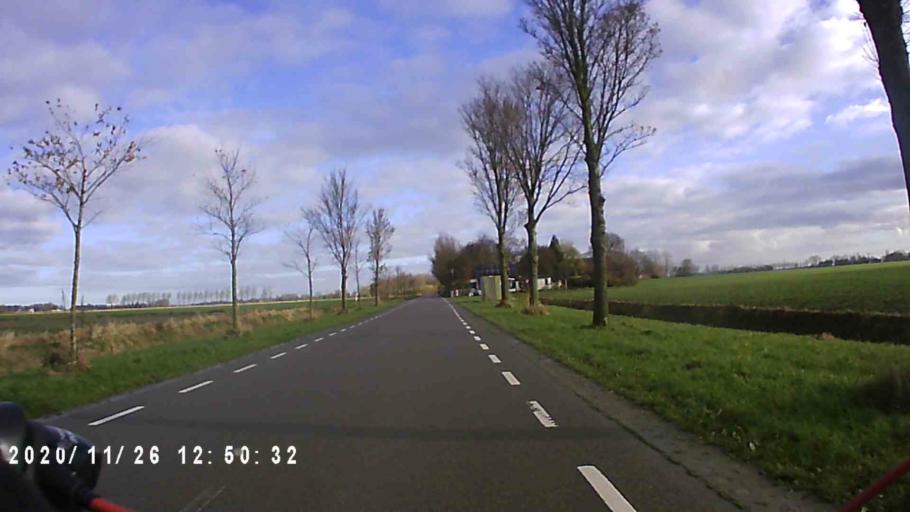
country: NL
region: Groningen
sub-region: Gemeente Appingedam
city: Appingedam
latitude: 53.3507
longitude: 6.7776
